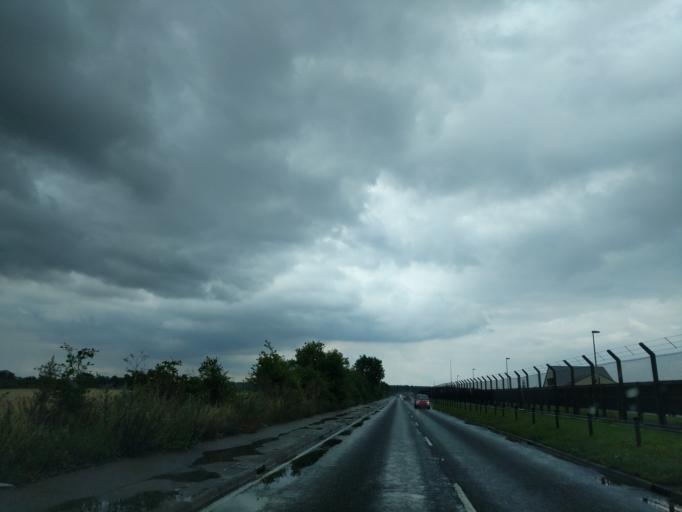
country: GB
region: England
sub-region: Suffolk
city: Lakenheath
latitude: 52.3632
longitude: 0.5026
